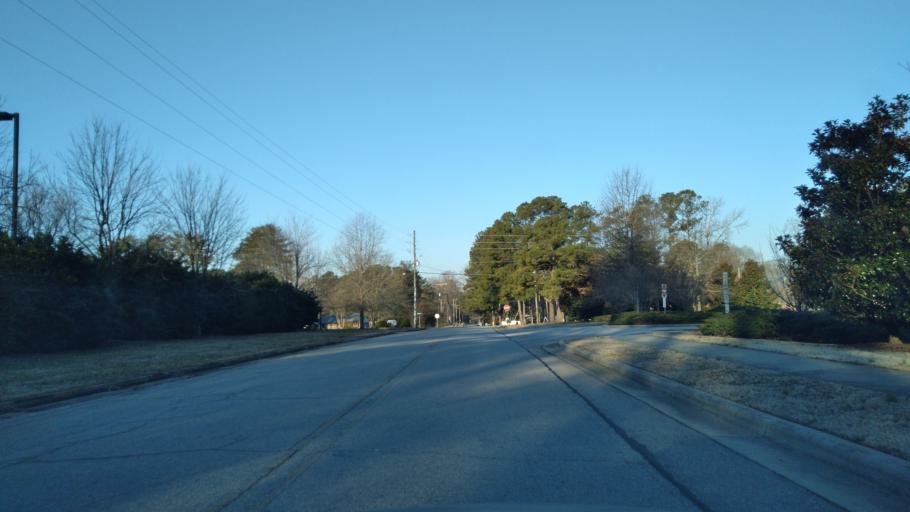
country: US
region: North Carolina
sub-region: Wake County
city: Garner
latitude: 35.6879
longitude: -78.6160
